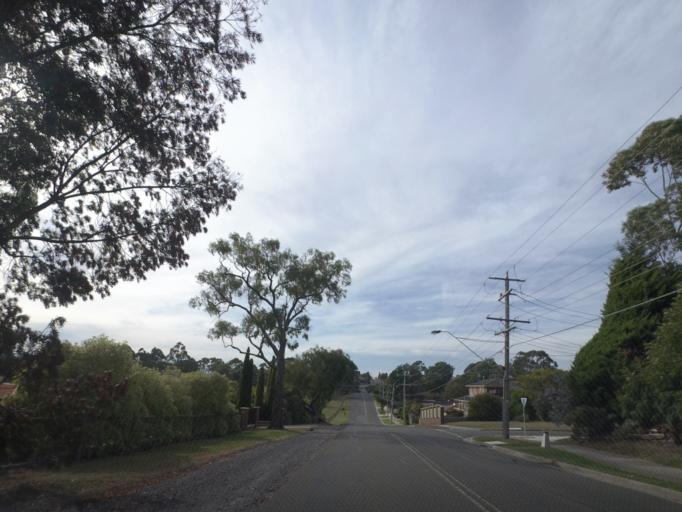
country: AU
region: Victoria
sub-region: Yarra Ranges
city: Chirnside Park
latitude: -37.7449
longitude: 145.3312
